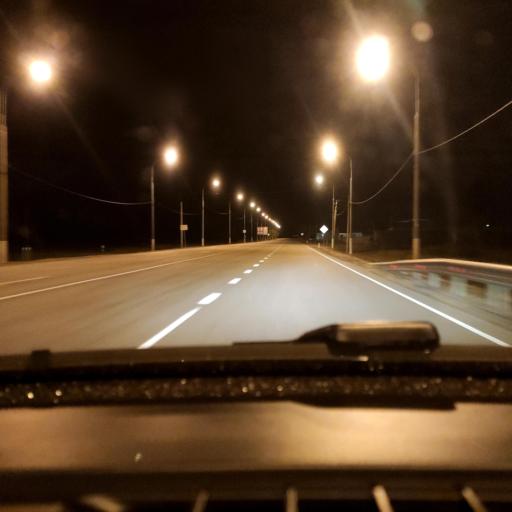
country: RU
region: Voronezj
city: Kashirskoye
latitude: 51.3907
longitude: 39.5668
